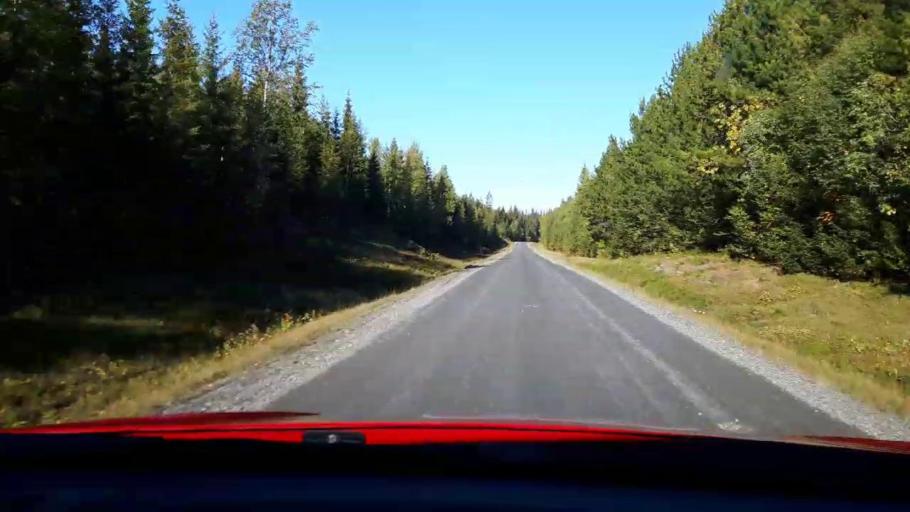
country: NO
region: Nord-Trondelag
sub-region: Lierne
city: Sandvika
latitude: 64.5289
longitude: 14.0483
